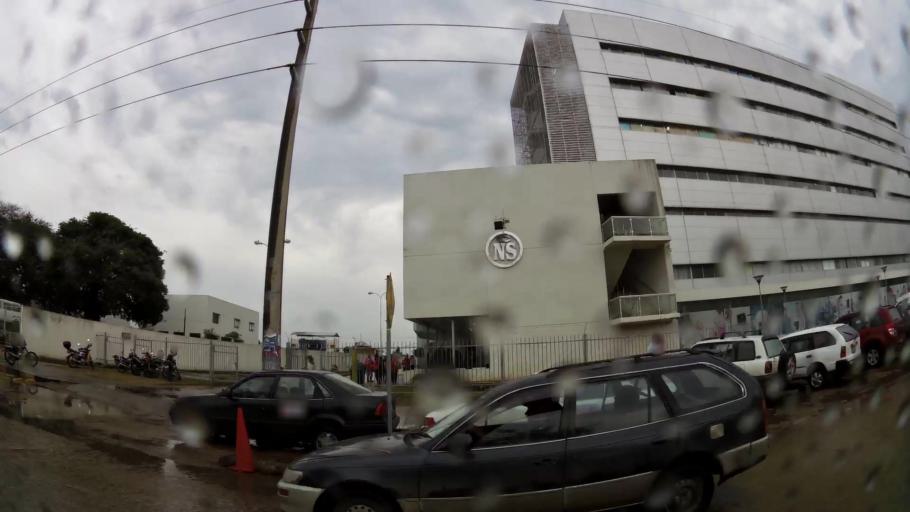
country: BO
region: Santa Cruz
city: Santa Cruz de la Sierra
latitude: -17.7667
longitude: -63.1558
